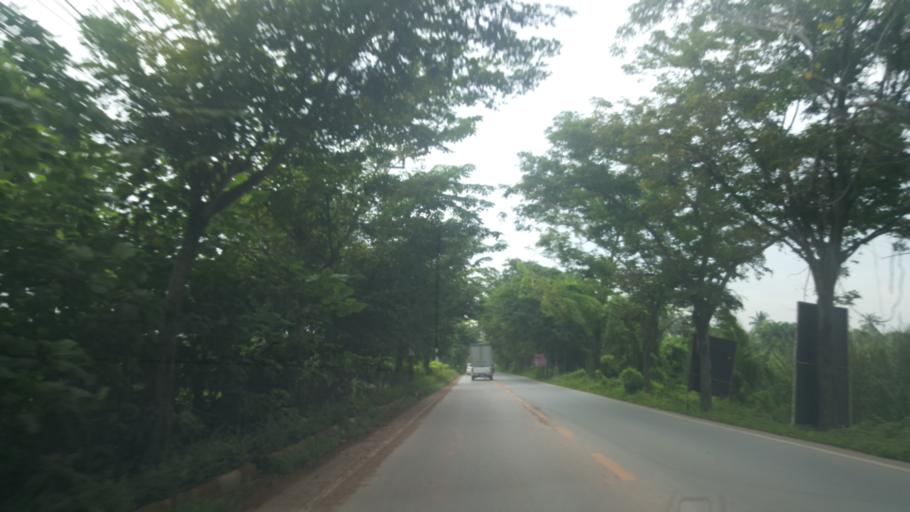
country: TH
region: Bangkok
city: Bang Khae
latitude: 13.6827
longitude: 100.3934
